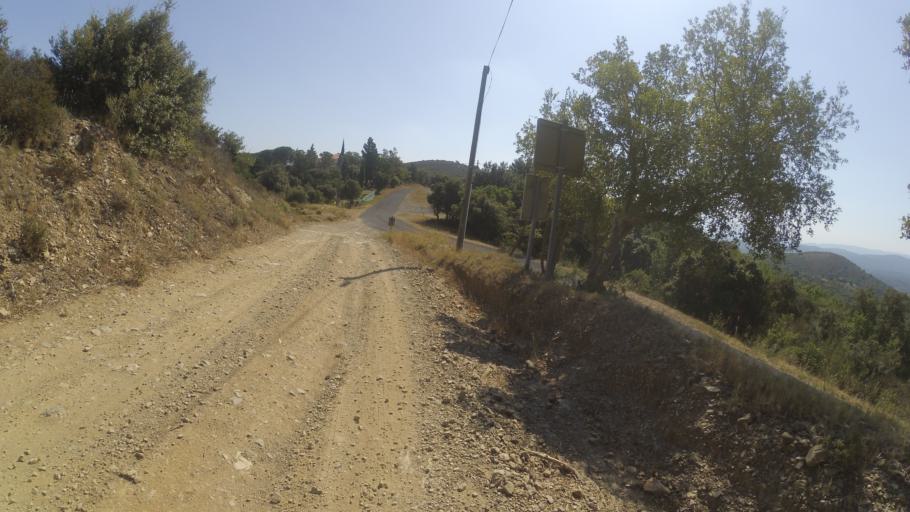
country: FR
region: Languedoc-Roussillon
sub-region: Departement des Pyrenees-Orientales
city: Thuir
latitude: 42.6147
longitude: 2.6821
